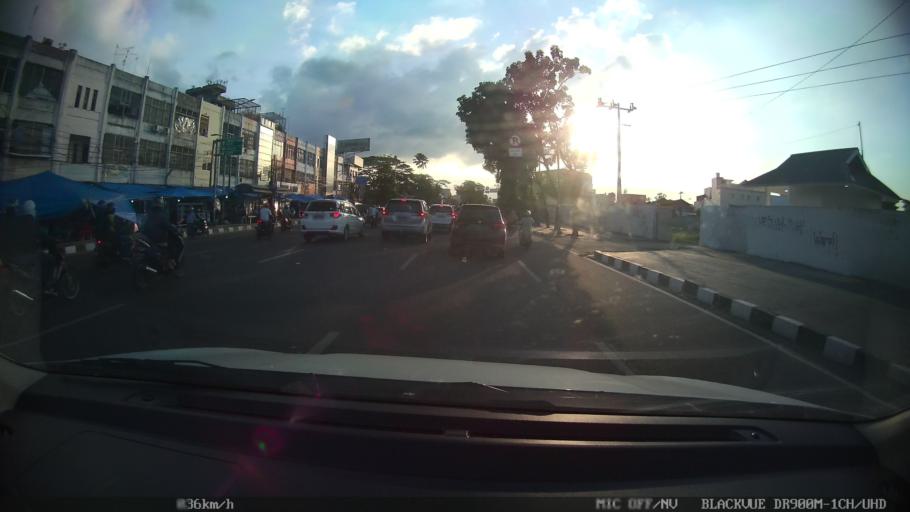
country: ID
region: North Sumatra
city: Medan
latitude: 3.5911
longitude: 98.6626
